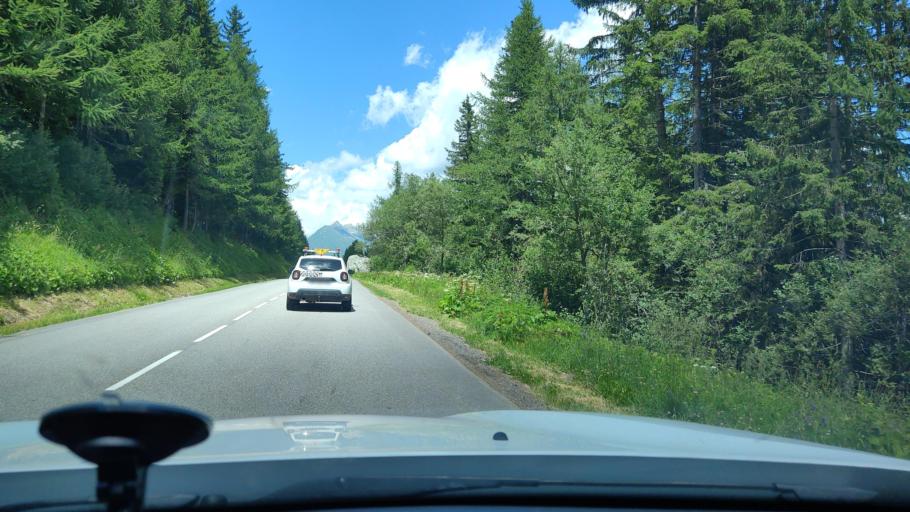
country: FR
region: Rhone-Alpes
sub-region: Departement de la Savoie
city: Seez
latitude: 45.5907
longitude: 6.8276
